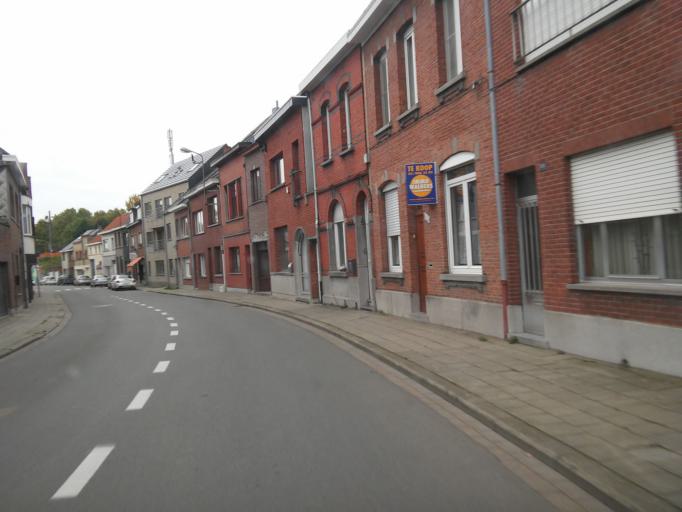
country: BE
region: Flanders
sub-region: Provincie Antwerpen
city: Willebroek
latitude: 51.0651
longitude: 4.3625
